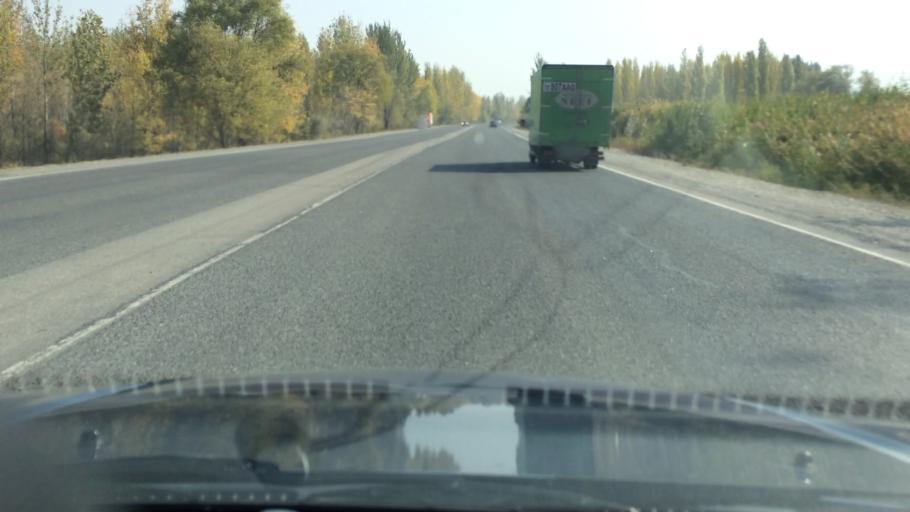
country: KG
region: Chuy
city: Ivanovka
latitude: 42.9390
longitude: 74.9804
